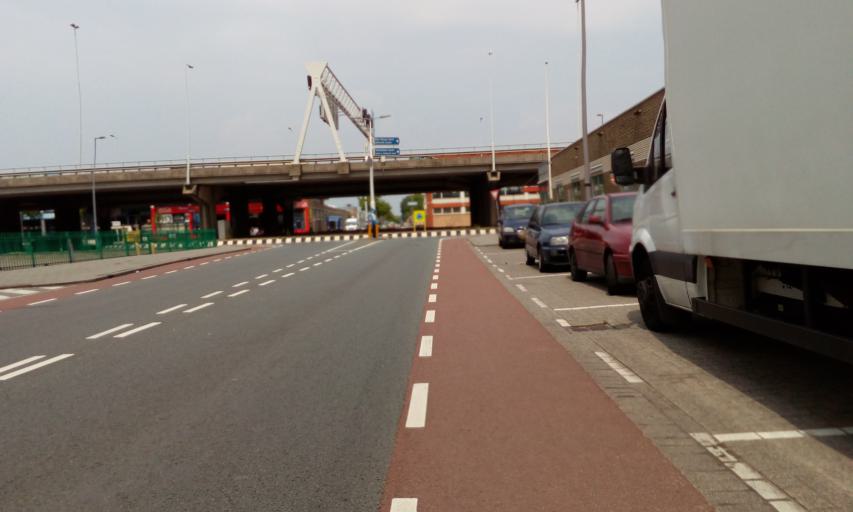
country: NL
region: South Holland
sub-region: Gemeente Rotterdam
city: Delfshaven
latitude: 51.9248
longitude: 4.4248
